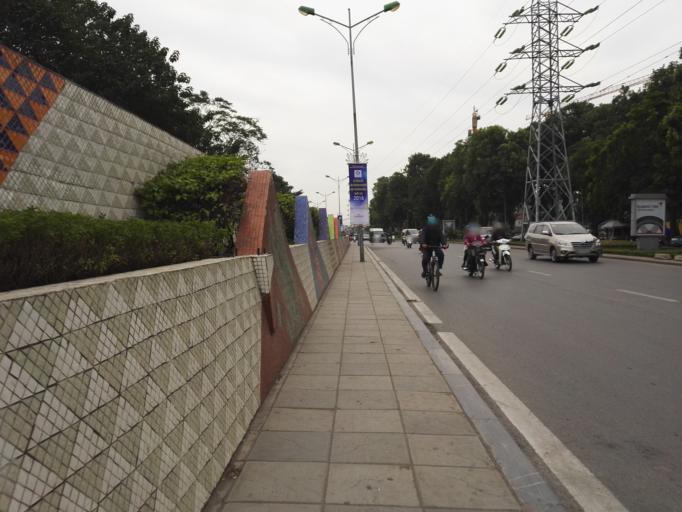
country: VN
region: Ha Noi
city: Hoan Kiem
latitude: 21.0461
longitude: 105.8447
